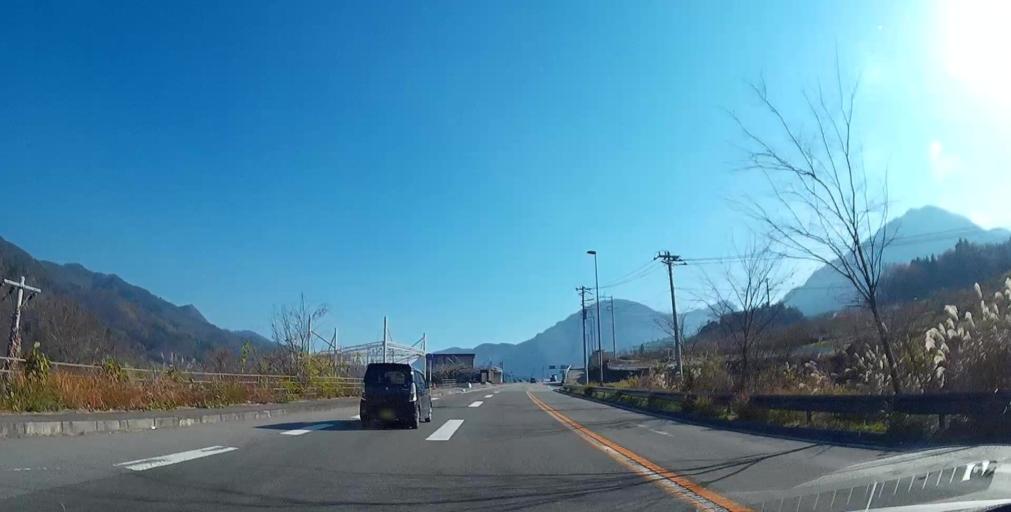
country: JP
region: Yamanashi
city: Isawa
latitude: 35.6102
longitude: 138.7001
